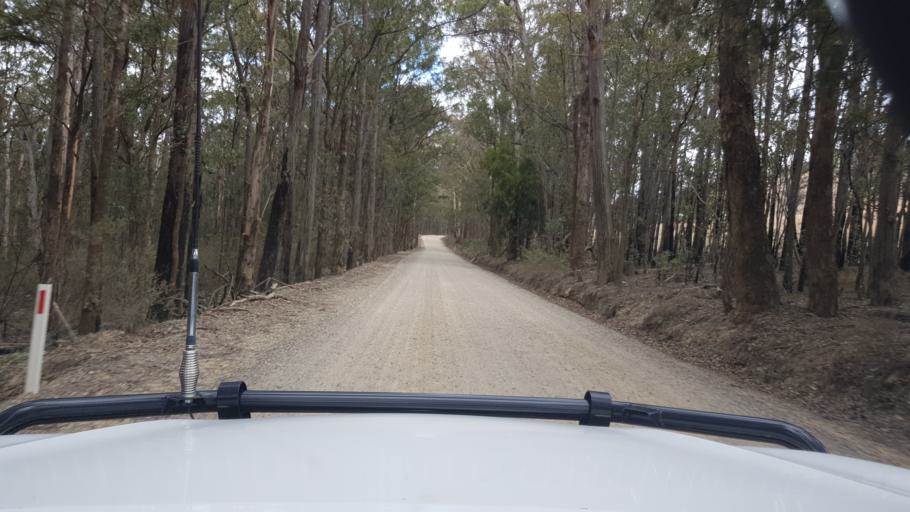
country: AU
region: Victoria
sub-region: East Gippsland
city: Bairnsdale
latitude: -37.6857
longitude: 147.5595
